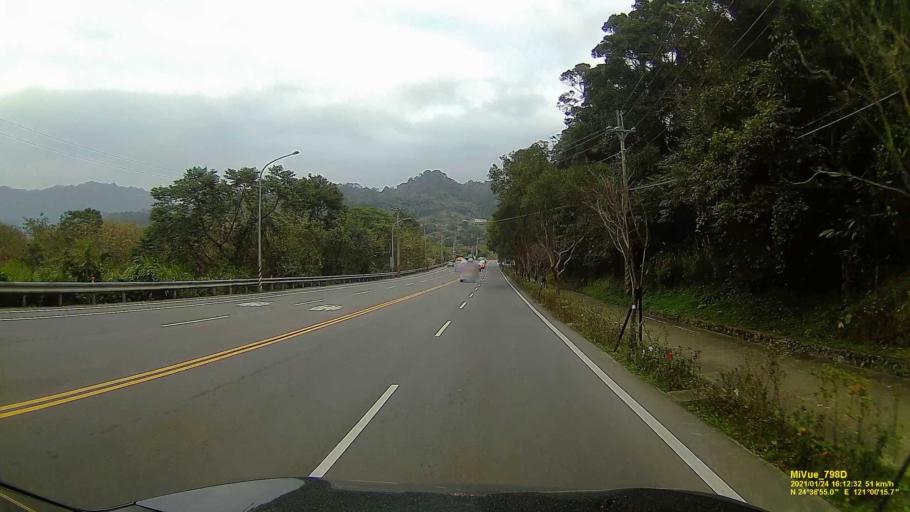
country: TW
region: Taiwan
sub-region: Miaoli
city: Miaoli
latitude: 24.6154
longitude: 121.0046
